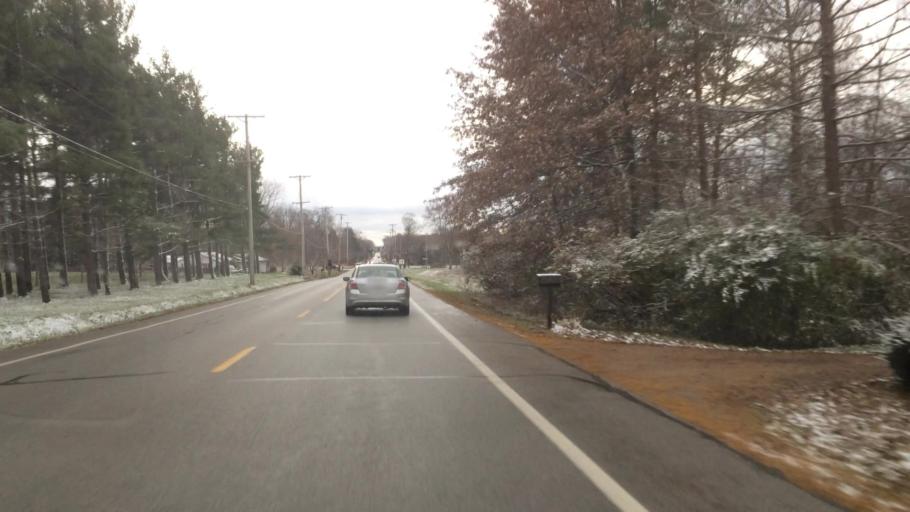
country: US
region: Ohio
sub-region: Summit County
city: Hudson
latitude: 41.2279
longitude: -81.4112
